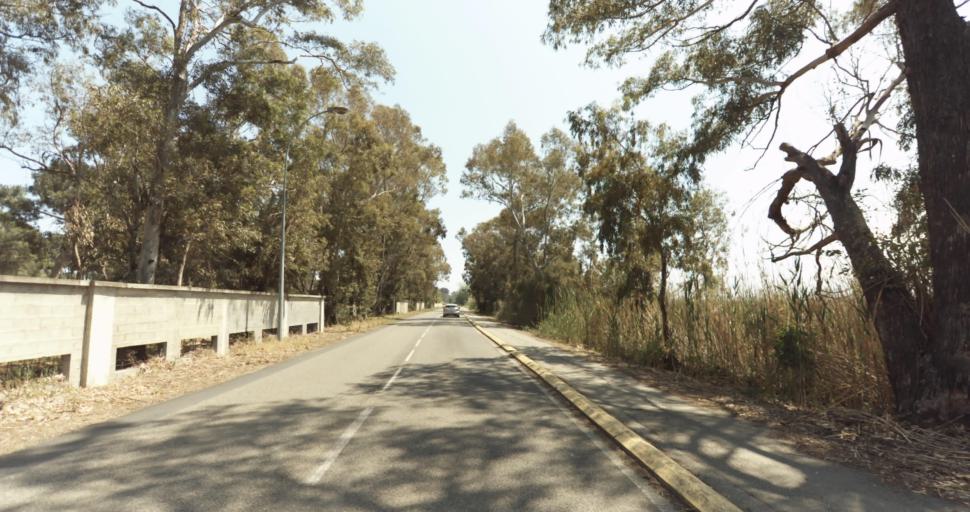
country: FR
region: Corsica
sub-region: Departement de la Haute-Corse
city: Biguglia
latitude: 42.6123
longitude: 9.4812
